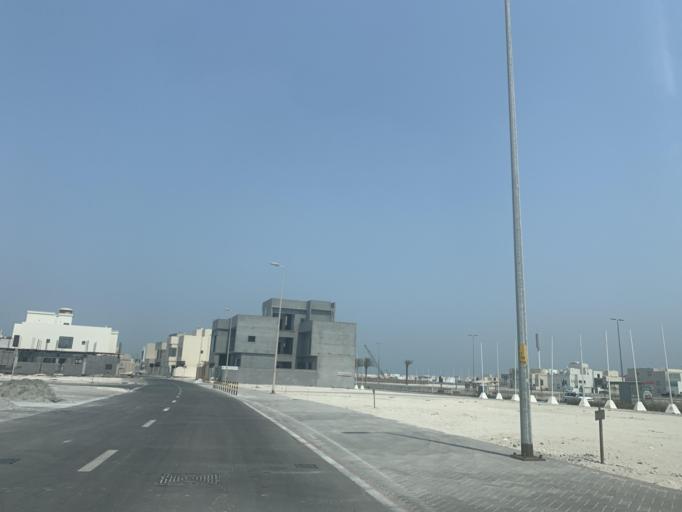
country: BH
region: Muharraq
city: Al Hadd
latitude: 26.2346
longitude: 50.6601
